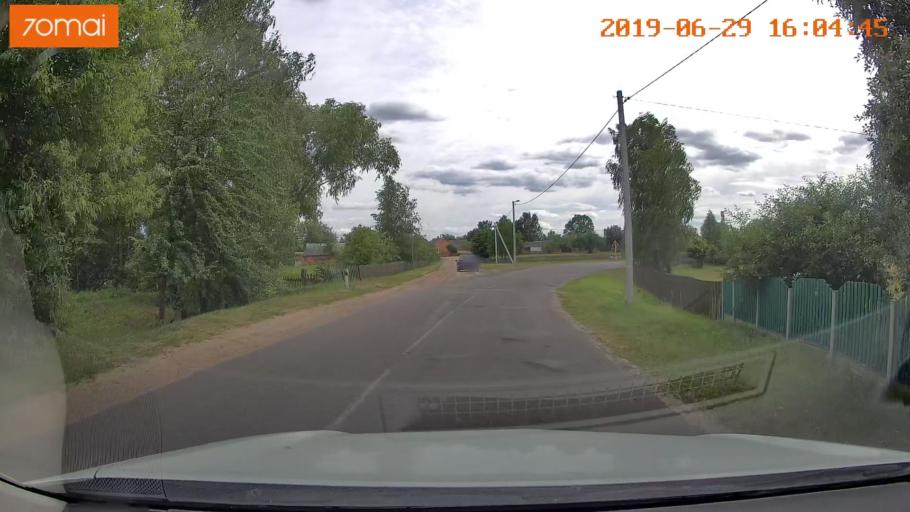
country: BY
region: Brest
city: Luninyets
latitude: 52.2200
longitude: 27.0245
